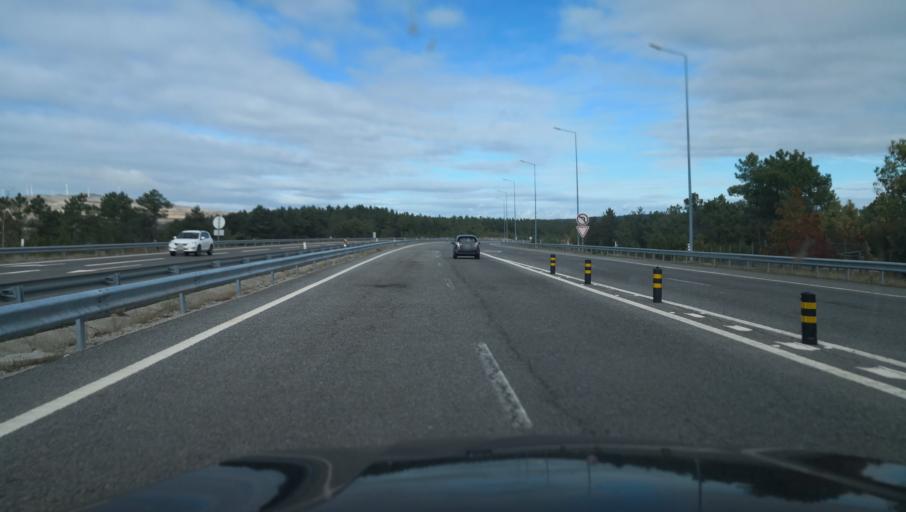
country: PT
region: Vila Real
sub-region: Vila Pouca de Aguiar
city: Vila Pouca de Aguiar
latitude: 41.5099
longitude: -7.6573
